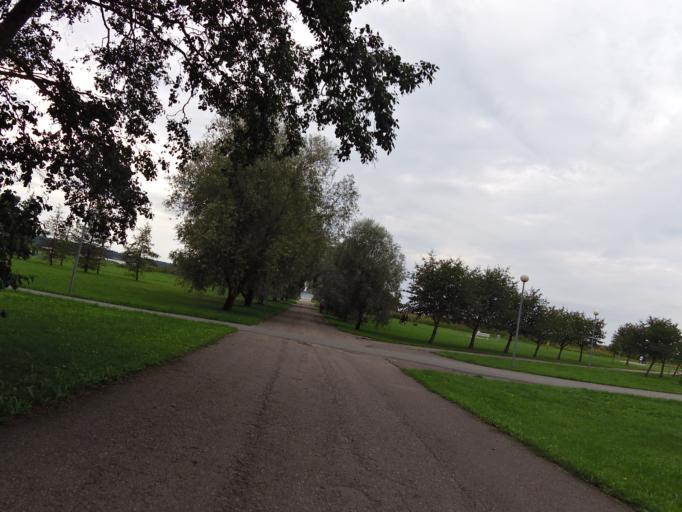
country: EE
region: Harju
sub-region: Tallinna linn
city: Tallinn
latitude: 59.4372
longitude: 24.6839
